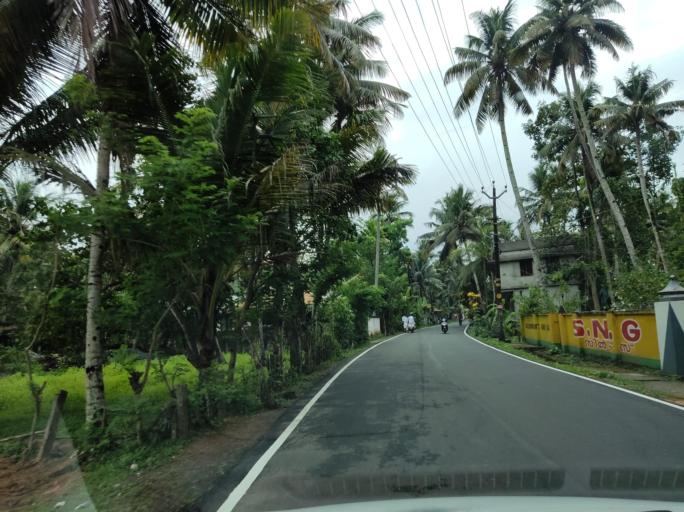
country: IN
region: Kerala
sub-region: Alappuzha
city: Kayankulam
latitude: 9.2708
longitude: 76.4026
